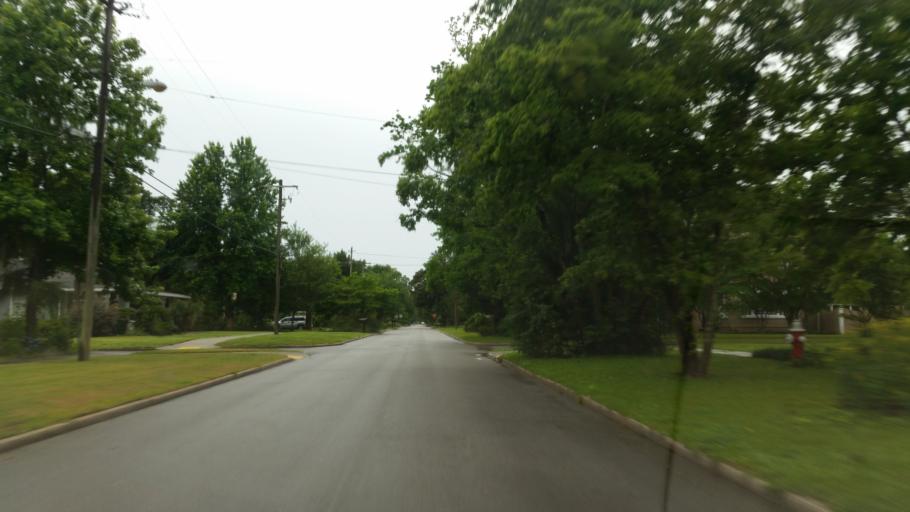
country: US
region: Florida
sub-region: Escambia County
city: East Pensacola Heights
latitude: 30.4236
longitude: -87.1929
